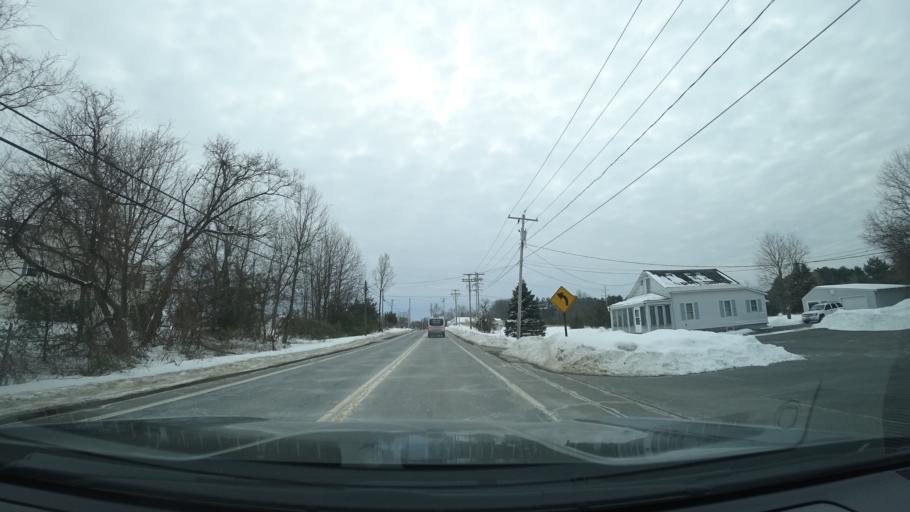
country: US
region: New York
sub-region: Saratoga County
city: South Glens Falls
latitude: 43.2876
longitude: -73.6246
